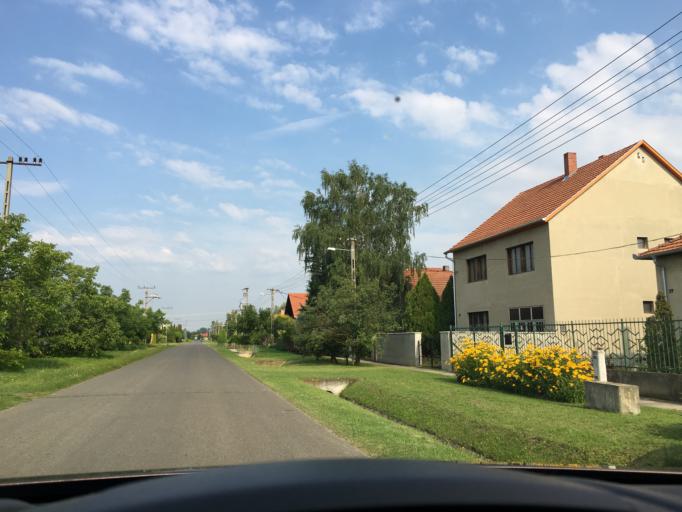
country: HU
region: Csongrad
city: Morahalom
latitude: 46.2105
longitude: 19.8808
